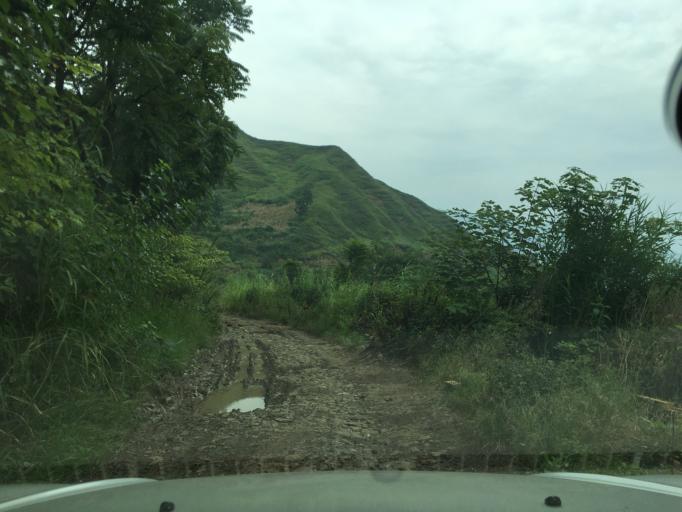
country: CN
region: Guizhou Sheng
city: Liupanshui
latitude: 26.0370
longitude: 105.1880
